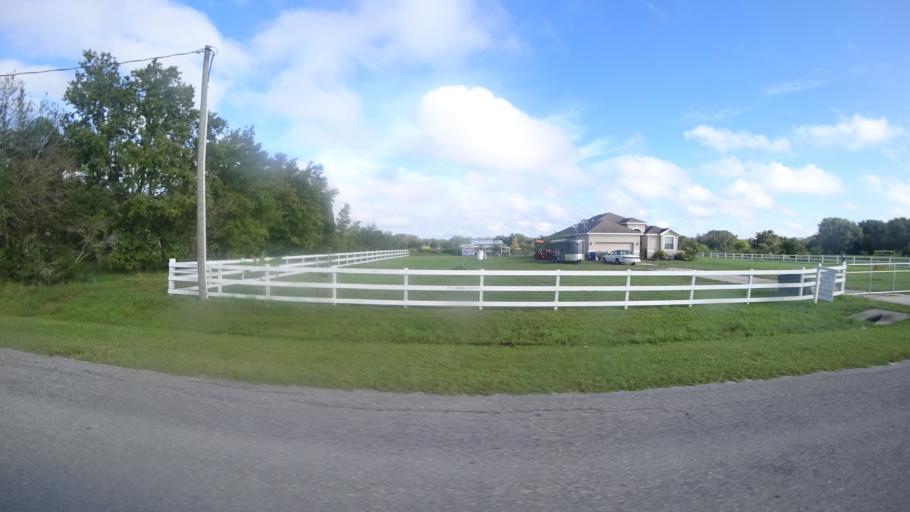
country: US
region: Florida
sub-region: Manatee County
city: Ellenton
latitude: 27.5574
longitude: -82.4043
